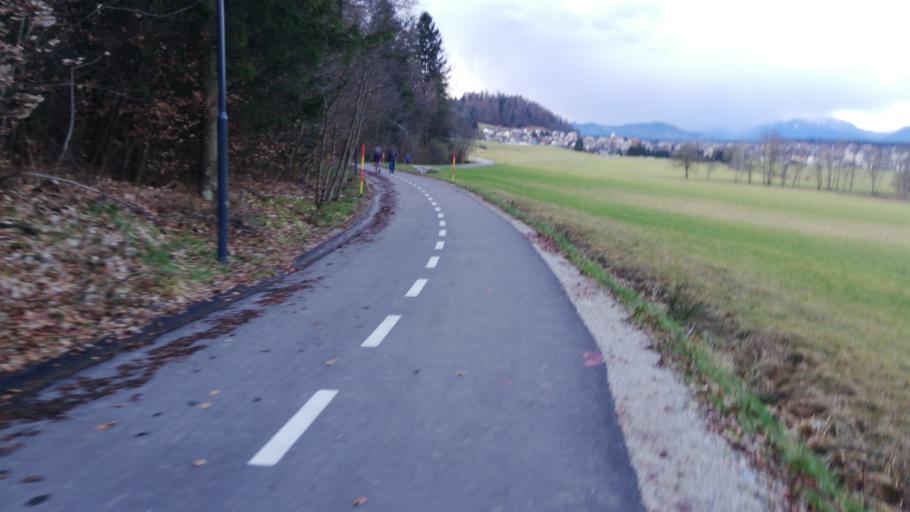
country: SI
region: Medvode
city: Medvode
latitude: 46.1234
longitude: 14.4209
